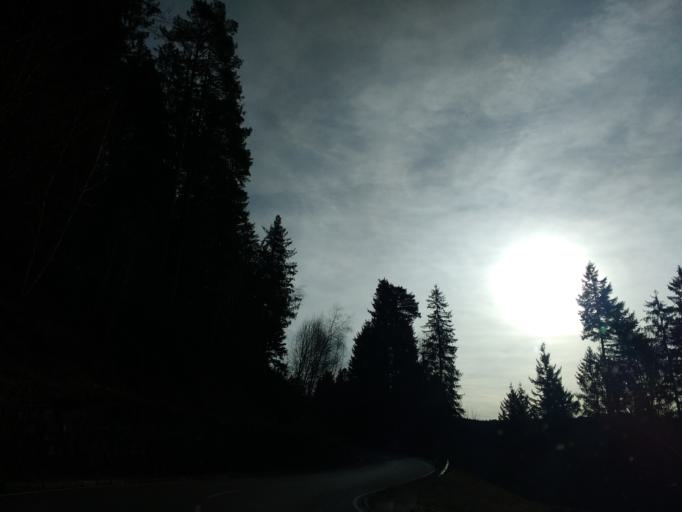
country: DE
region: Baden-Wuerttemberg
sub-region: Karlsruhe Region
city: Bad Rippoldsau-Schapbach
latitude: 48.4533
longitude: 8.2897
